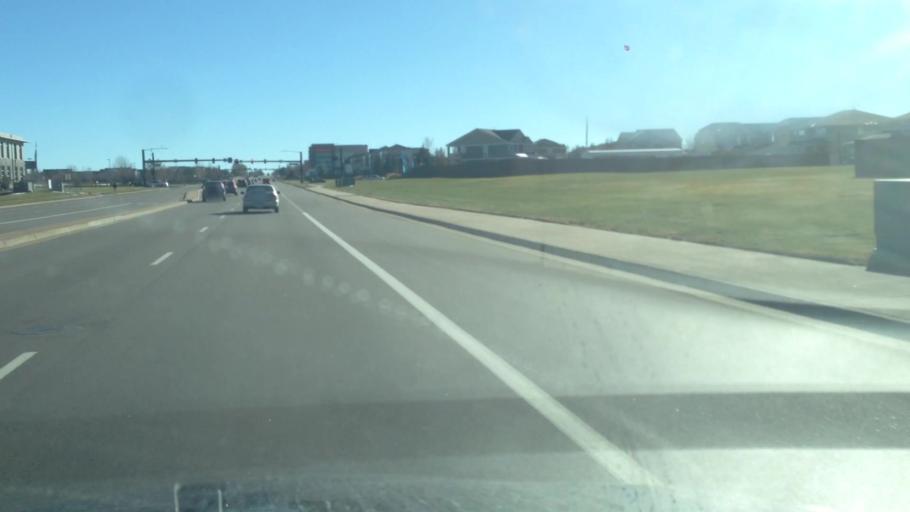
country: US
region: Colorado
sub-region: Douglas County
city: Stonegate
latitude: 39.5455
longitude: -104.7936
